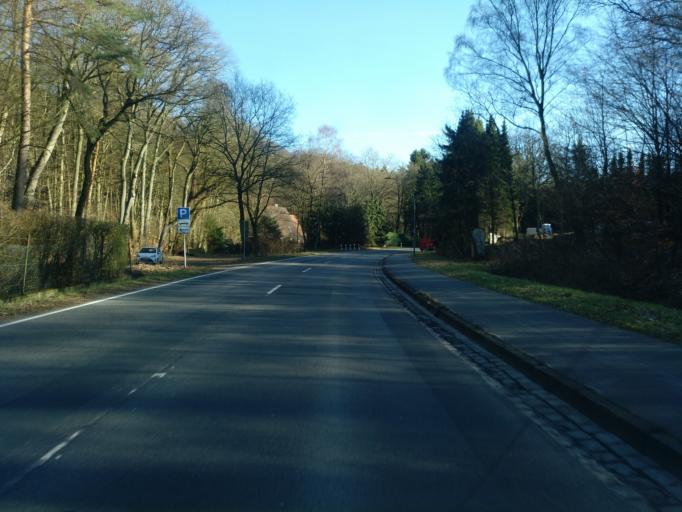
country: DE
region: Hamburg
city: Harburg
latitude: 53.4530
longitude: 9.9036
